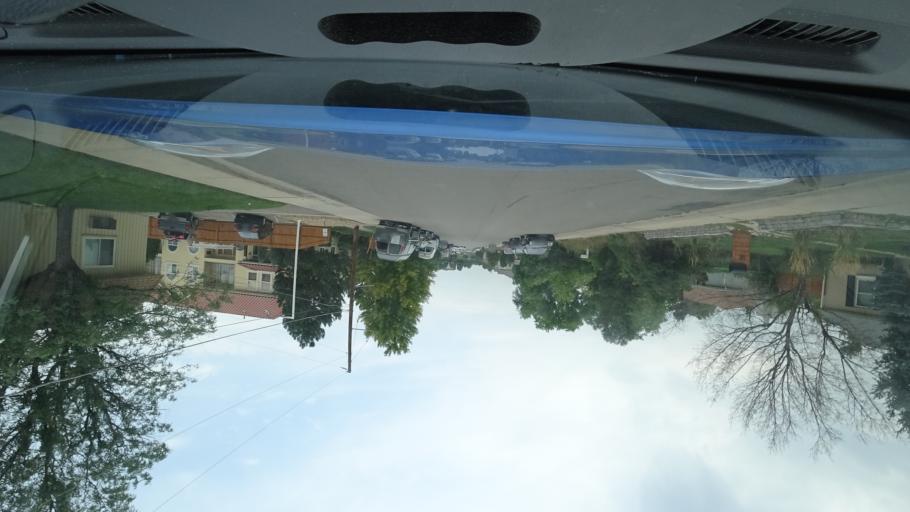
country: US
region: Colorado
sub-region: Arapahoe County
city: Glendale
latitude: 39.7007
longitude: -104.9141
